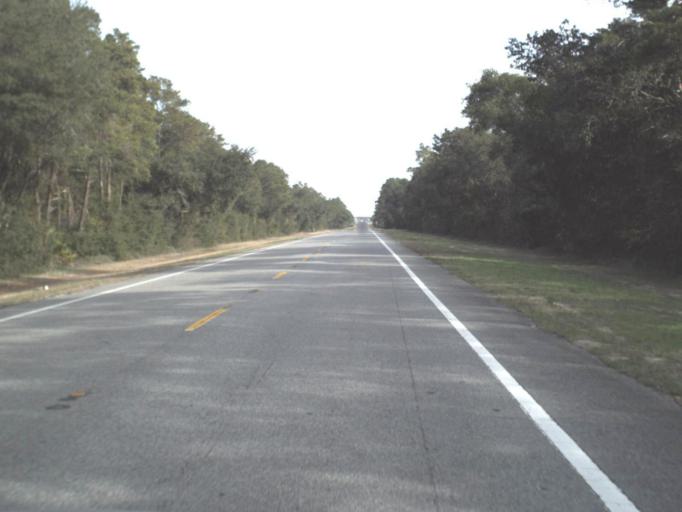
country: US
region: Florida
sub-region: Bay County
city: Mexico Beach
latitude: 29.9603
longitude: -85.4390
